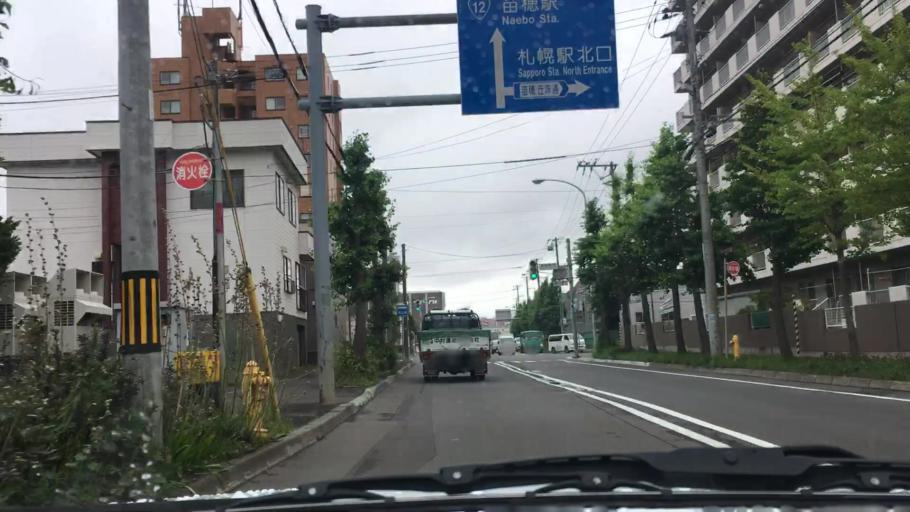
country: JP
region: Hokkaido
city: Sapporo
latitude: 43.0739
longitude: 141.3832
